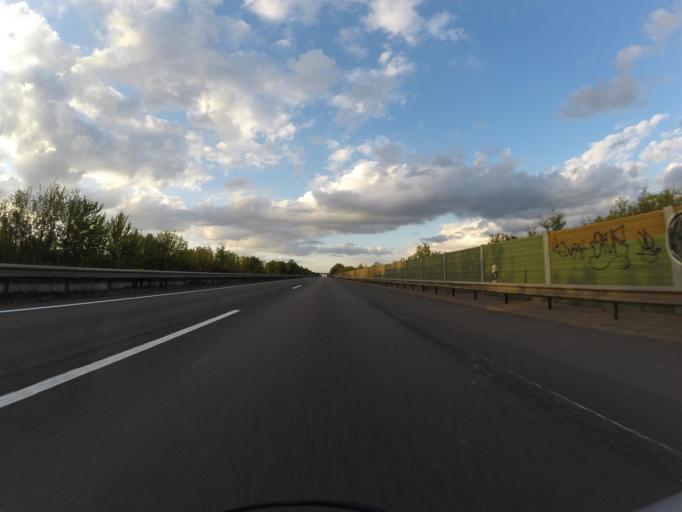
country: DE
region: Rheinland-Pfalz
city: Alzey
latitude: 49.7407
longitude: 8.0842
